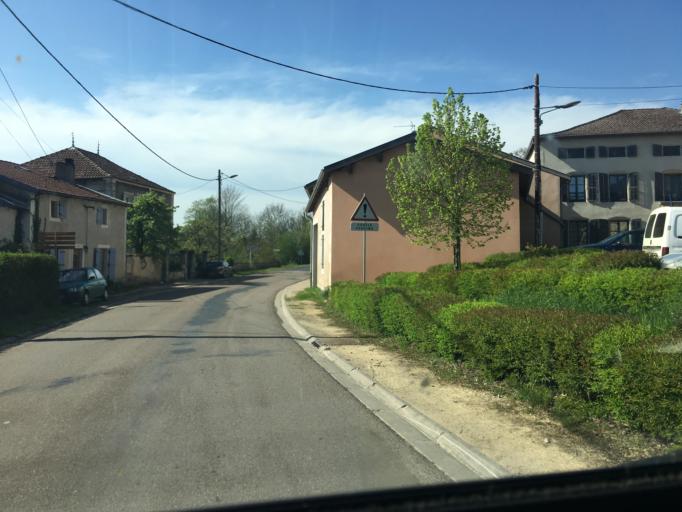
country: FR
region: Lorraine
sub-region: Departement de la Meuse
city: Vigneulles-les-Hattonchatel
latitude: 48.9143
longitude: 5.6706
